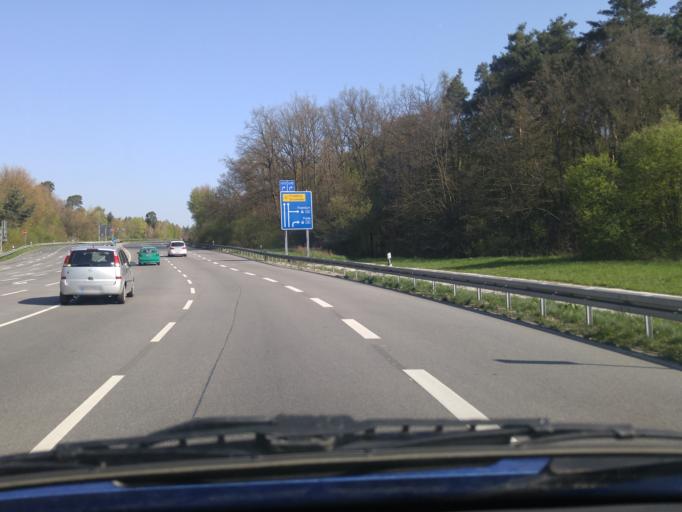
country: DE
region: Hesse
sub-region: Regierungsbezirk Darmstadt
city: Hanau am Main
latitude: 50.1512
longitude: 8.9091
